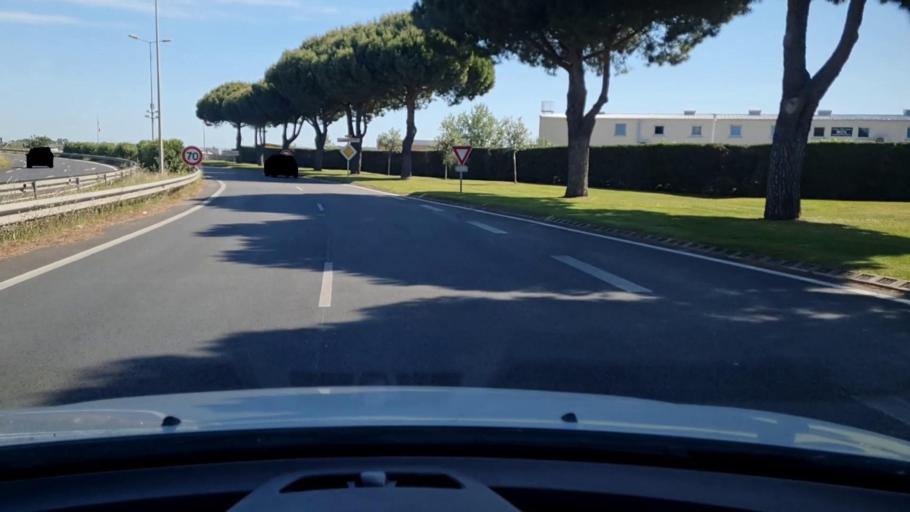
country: FR
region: Languedoc-Roussillon
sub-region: Departement du Gard
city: Le Grau-du-Roi
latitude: 43.5421
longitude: 4.1352
